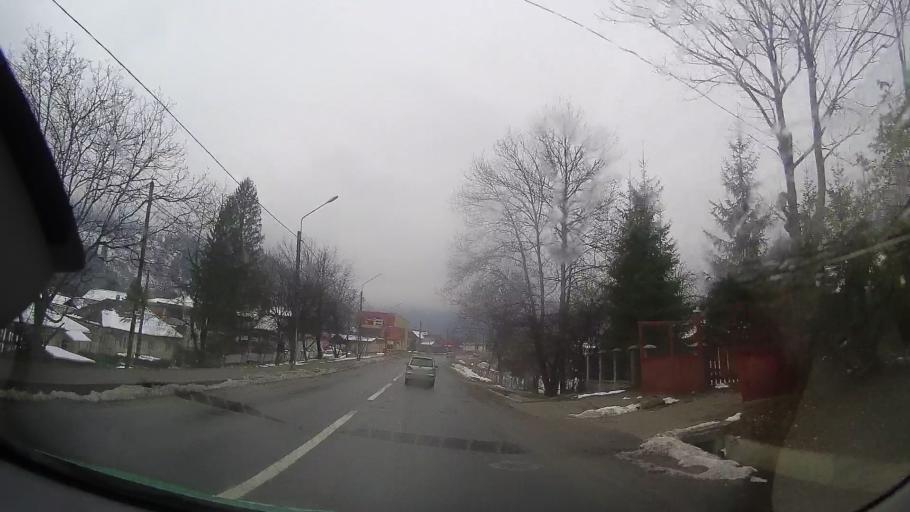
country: RO
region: Neamt
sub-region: Comuna Bicaz
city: Dodeni
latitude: 46.9038
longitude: 26.1108
